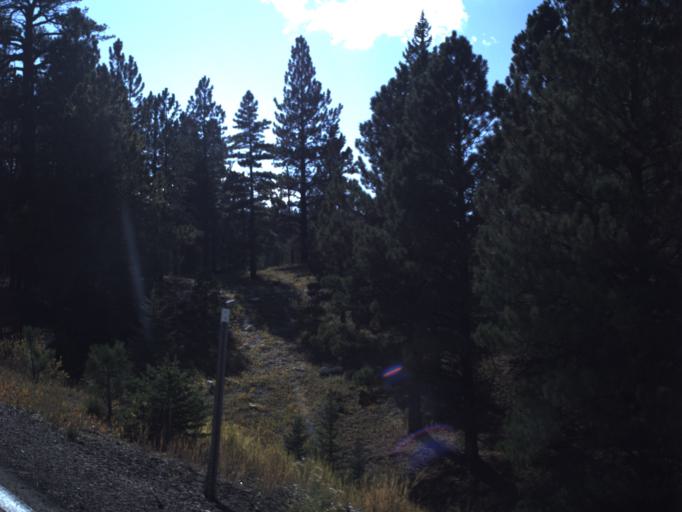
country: US
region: Utah
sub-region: Iron County
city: Parowan
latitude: 37.6968
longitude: -112.6632
